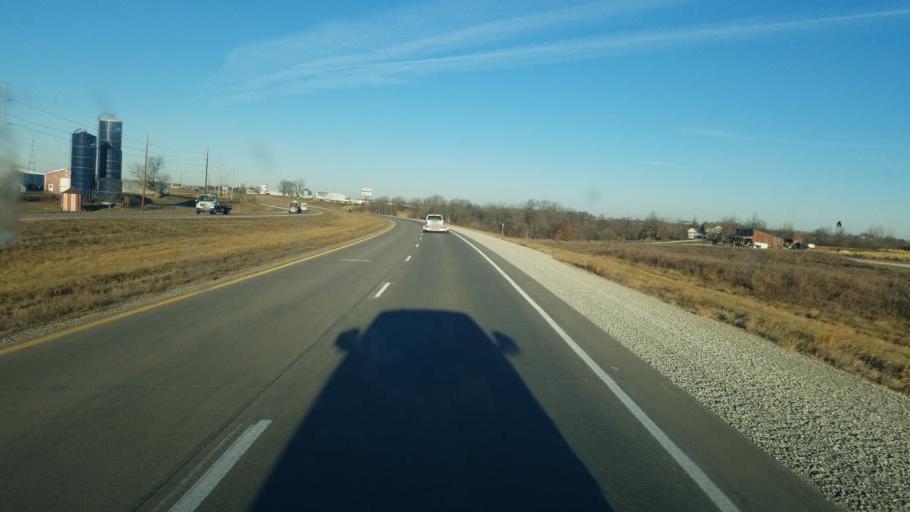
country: US
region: Iowa
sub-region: Marion County
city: Pella
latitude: 41.3850
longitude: -92.8238
